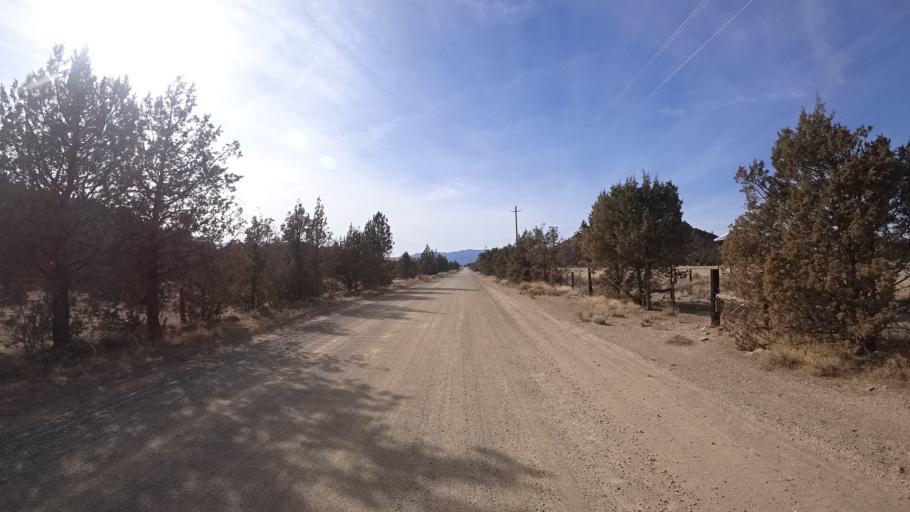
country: US
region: California
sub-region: Siskiyou County
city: Montague
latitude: 41.5819
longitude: -122.4529
